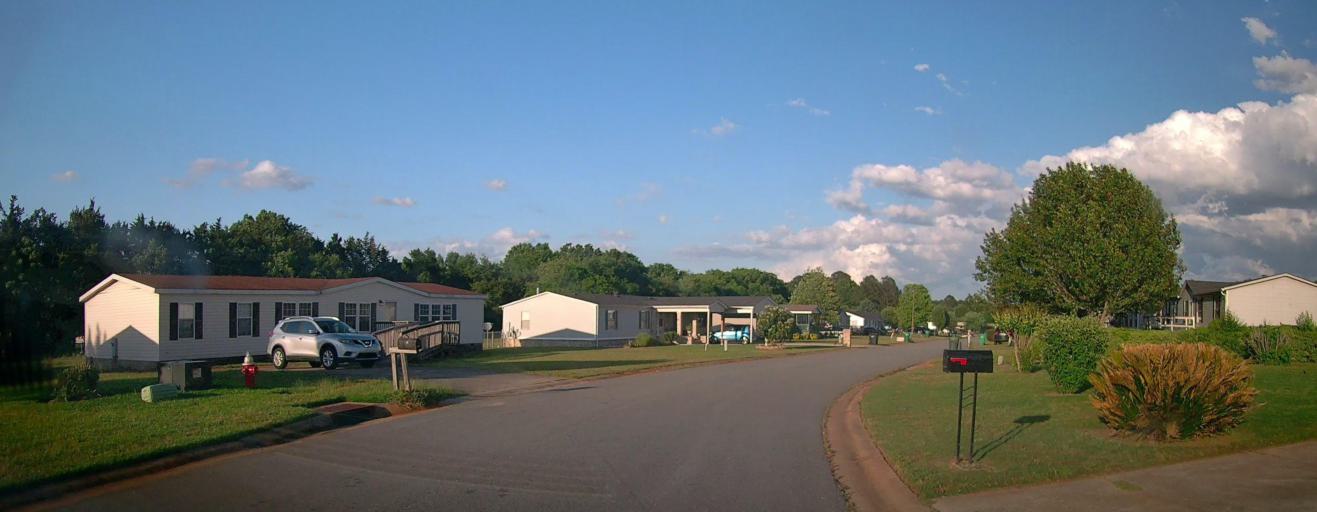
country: US
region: Georgia
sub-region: Peach County
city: Byron
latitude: 32.6427
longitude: -83.7273
